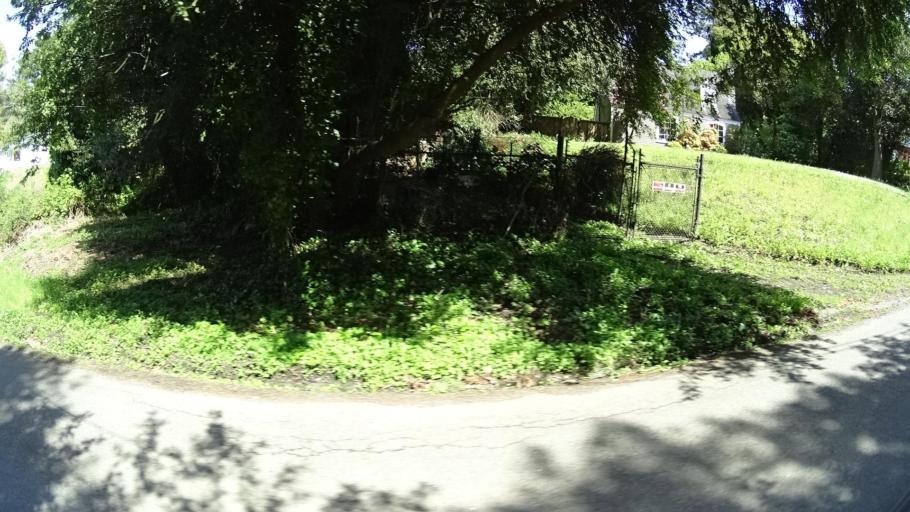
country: US
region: California
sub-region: Humboldt County
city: Fortuna
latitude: 40.5636
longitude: -124.1403
